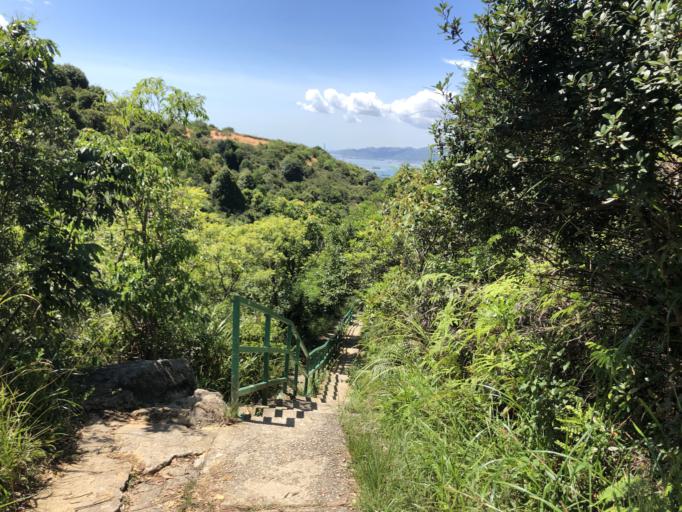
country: HK
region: Tuen Mun
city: Tuen Mun
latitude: 22.2822
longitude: 113.9833
